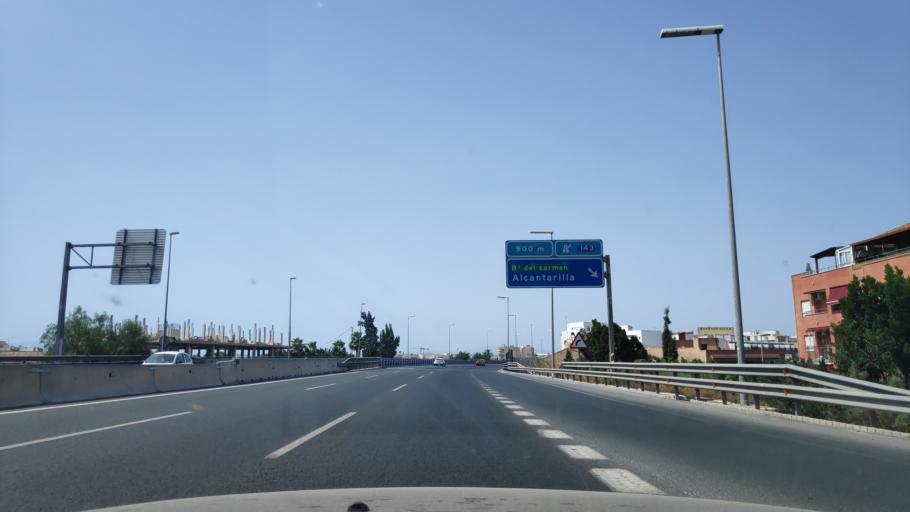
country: ES
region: Murcia
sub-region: Murcia
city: Murcia
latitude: 37.9682
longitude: -1.1376
